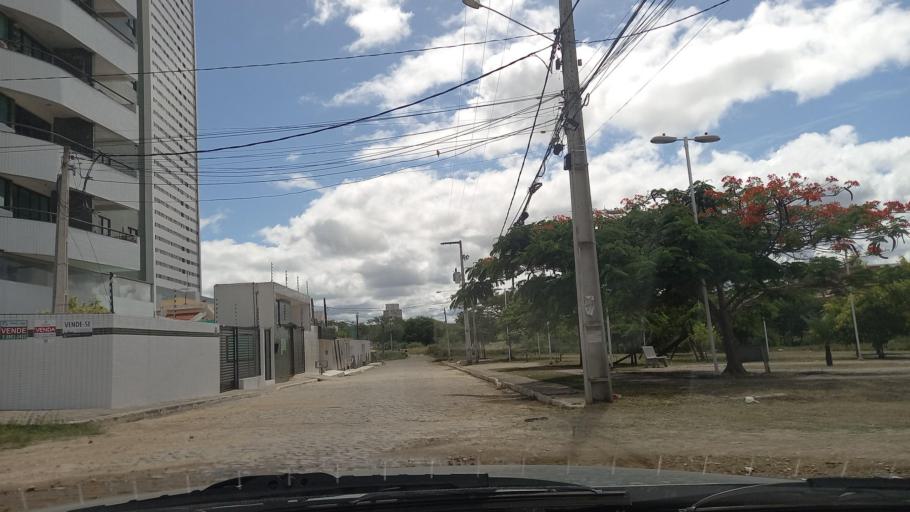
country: BR
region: Pernambuco
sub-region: Caruaru
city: Caruaru
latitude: -8.2666
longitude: -35.9622
